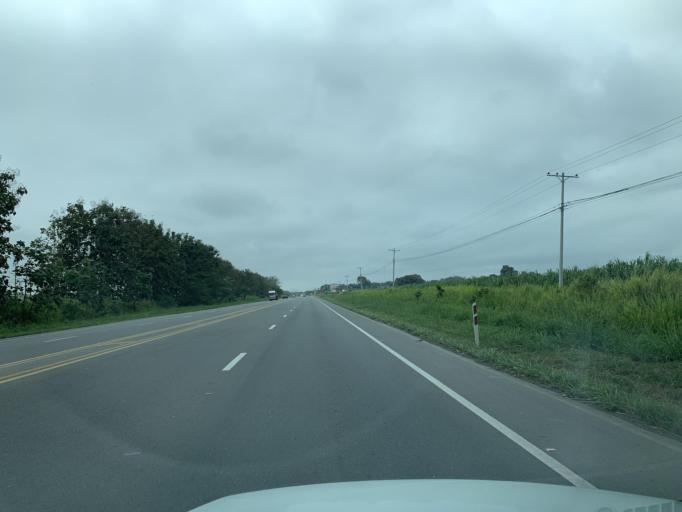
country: EC
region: Guayas
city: Coronel Marcelino Mariduena
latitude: -2.3124
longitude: -79.4745
